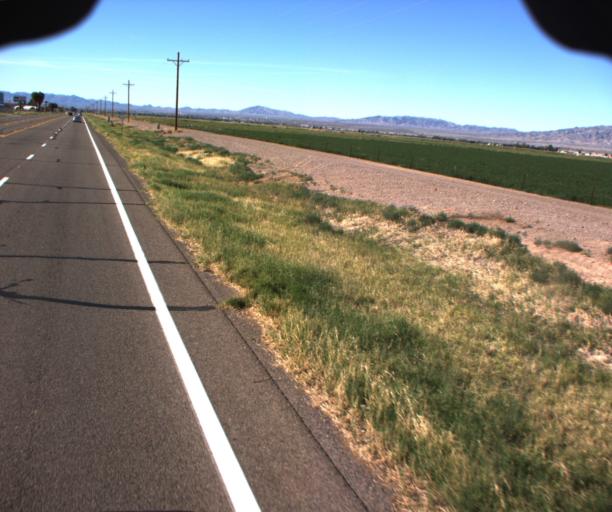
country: US
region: Arizona
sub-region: Mohave County
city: Willow Valley
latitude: 34.9064
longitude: -114.5980
